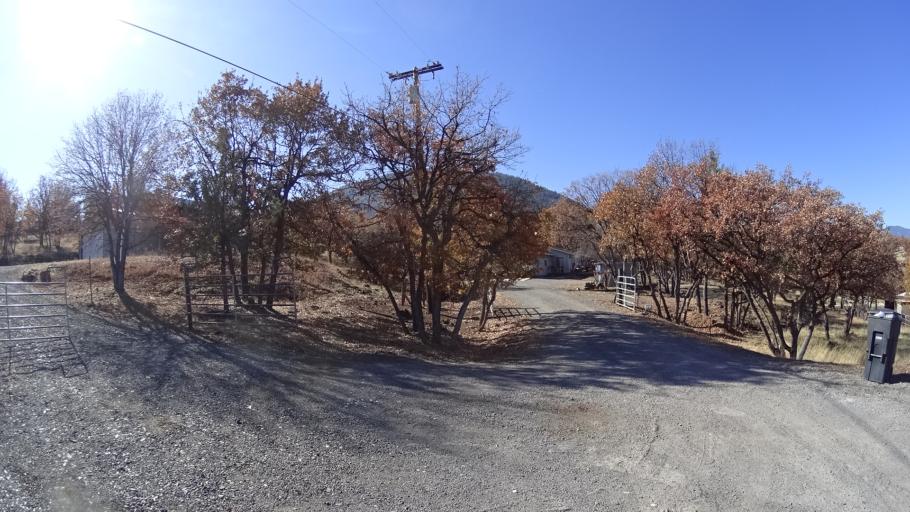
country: US
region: California
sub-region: Siskiyou County
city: Montague
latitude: 41.8788
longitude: -122.4851
